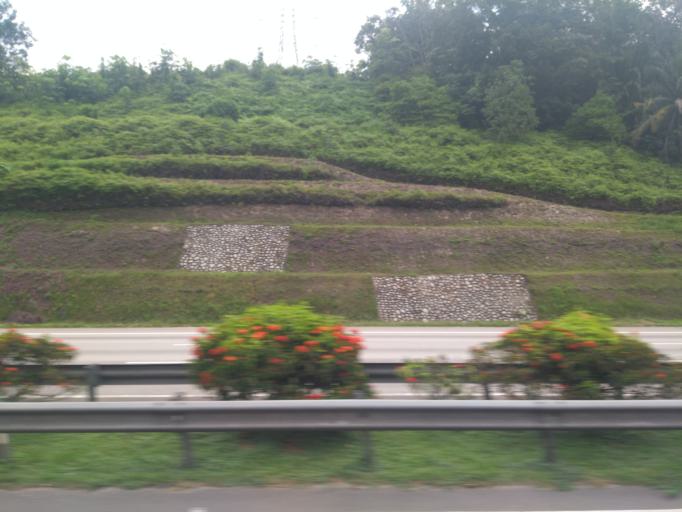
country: MY
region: Negeri Sembilan
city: Seremban
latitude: 2.6422
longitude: 101.9943
